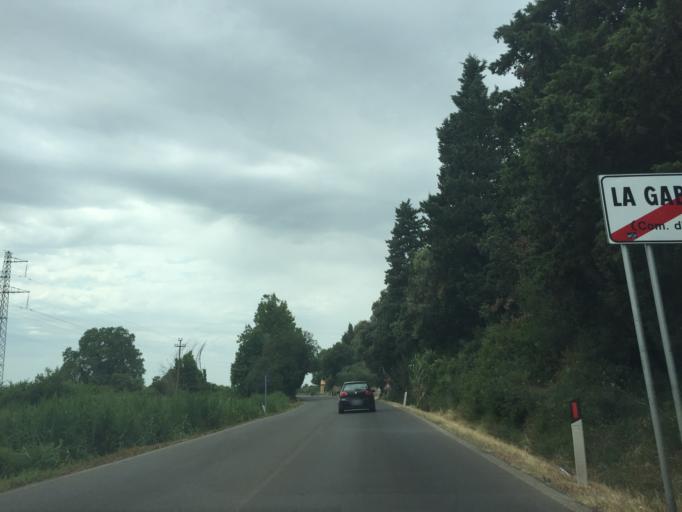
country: IT
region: Tuscany
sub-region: Province of Pisa
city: Gabella
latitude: 43.7261
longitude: 10.4904
